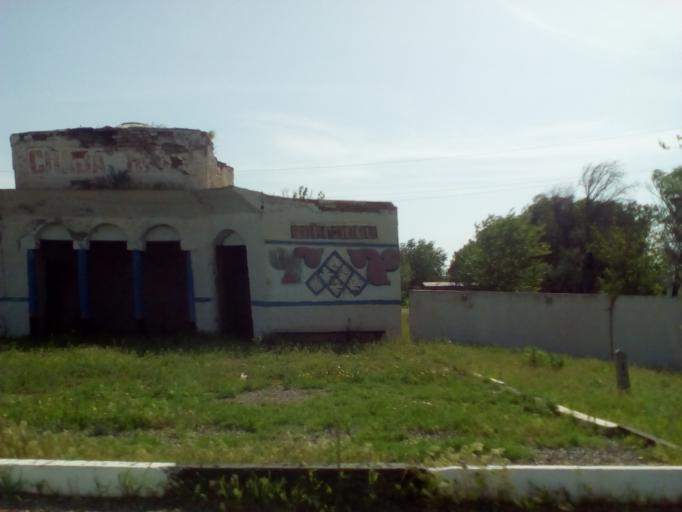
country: KZ
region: Ongtustik Qazaqstan
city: Shayan
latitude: 43.0465
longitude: 69.3898
